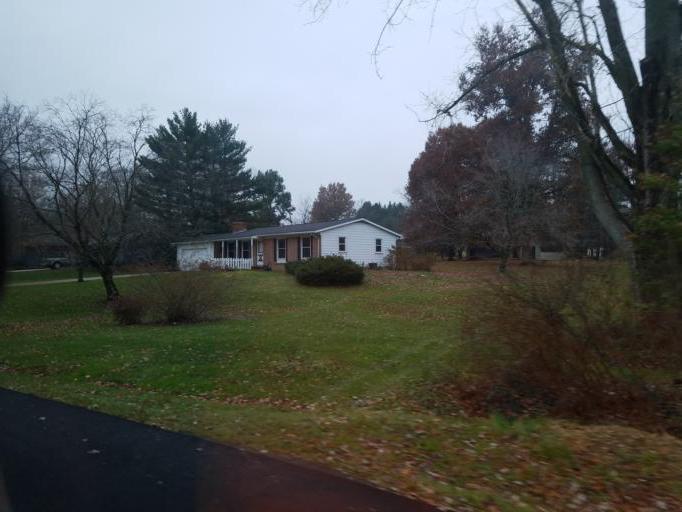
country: US
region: Ohio
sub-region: Richland County
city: Lexington
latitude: 40.7005
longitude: -82.5277
